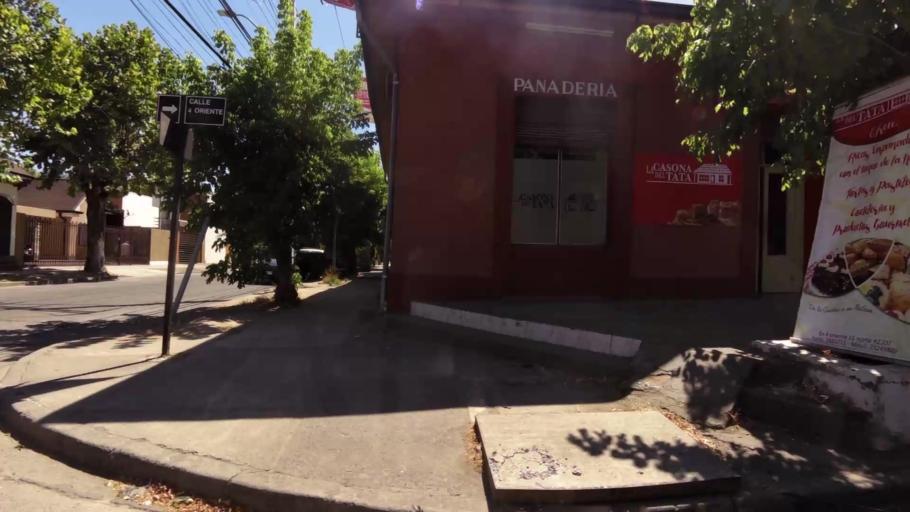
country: CL
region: Maule
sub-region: Provincia de Talca
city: Talca
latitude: -35.4131
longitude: -71.6599
